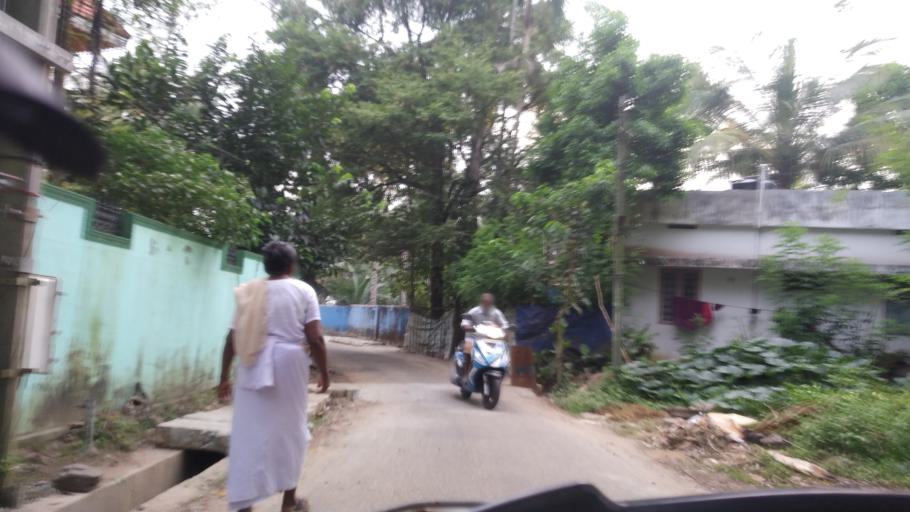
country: IN
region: Kerala
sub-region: Thrissur District
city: Kodungallur
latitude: 10.1350
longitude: 76.1992
